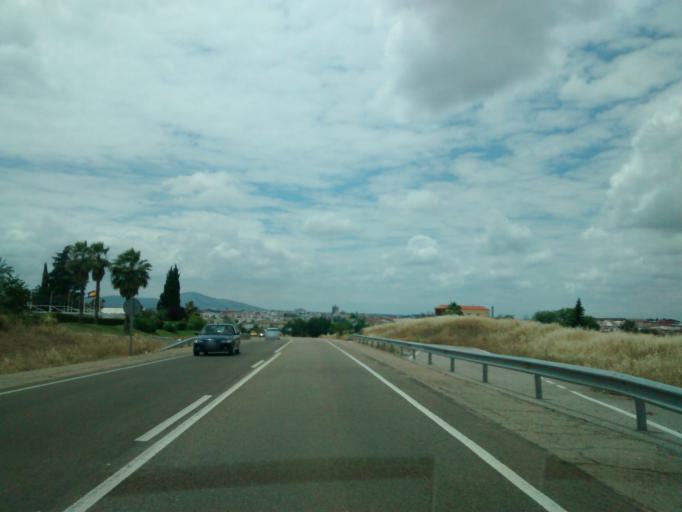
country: ES
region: Extremadura
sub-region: Provincia de Badajoz
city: Merida
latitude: 38.9304
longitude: -6.3157
